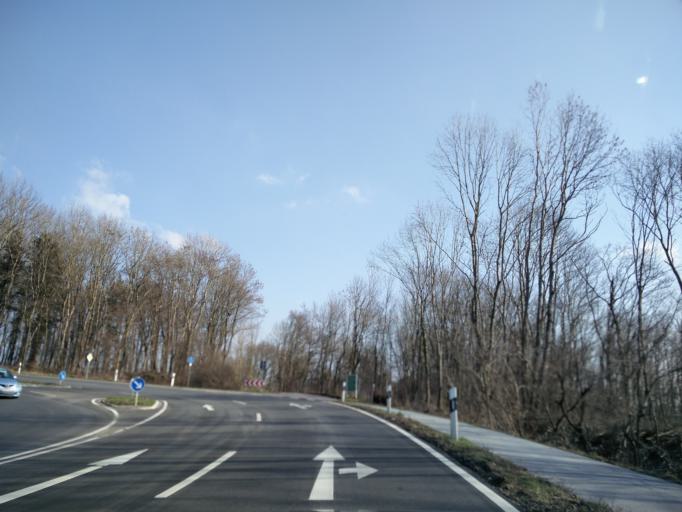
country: DE
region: North Rhine-Westphalia
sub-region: Regierungsbezirk Detmold
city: Buren
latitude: 51.5629
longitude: 8.5582
